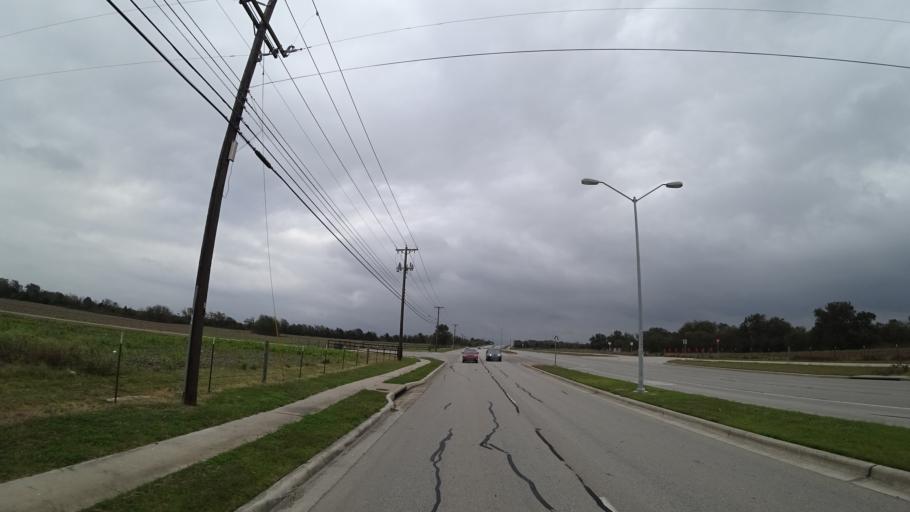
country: US
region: Texas
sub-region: Travis County
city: Pflugerville
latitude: 30.4316
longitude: -97.6031
